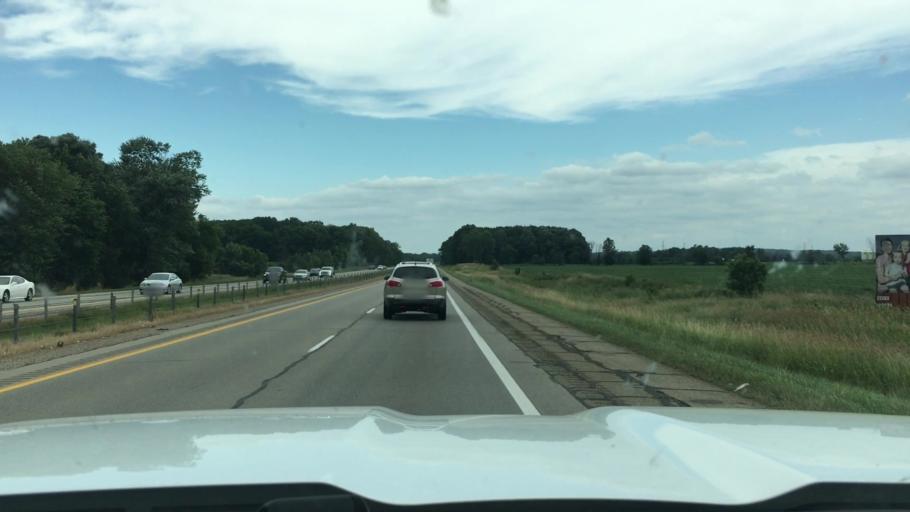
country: US
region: Michigan
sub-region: Allegan County
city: Wayland
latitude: 42.7423
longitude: -85.6732
